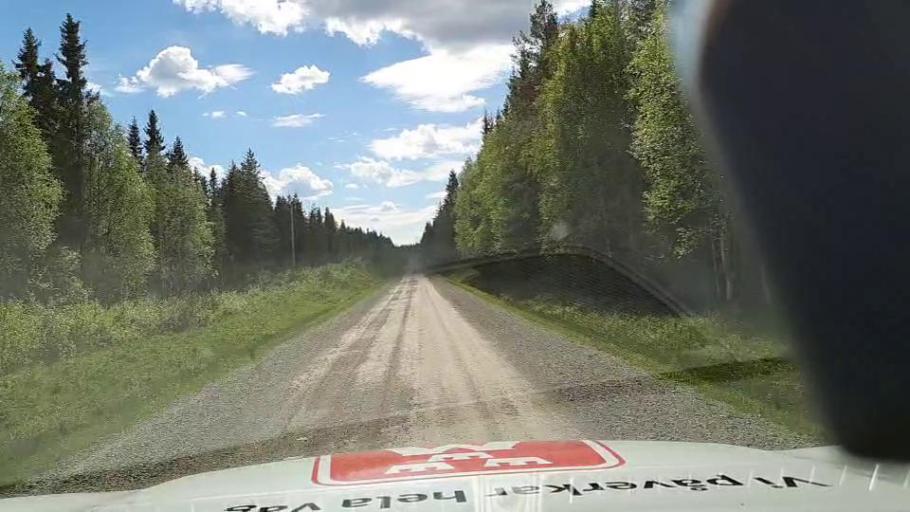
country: SE
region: Jaemtland
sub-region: Stroemsunds Kommun
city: Stroemsund
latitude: 64.5370
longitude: 15.6003
